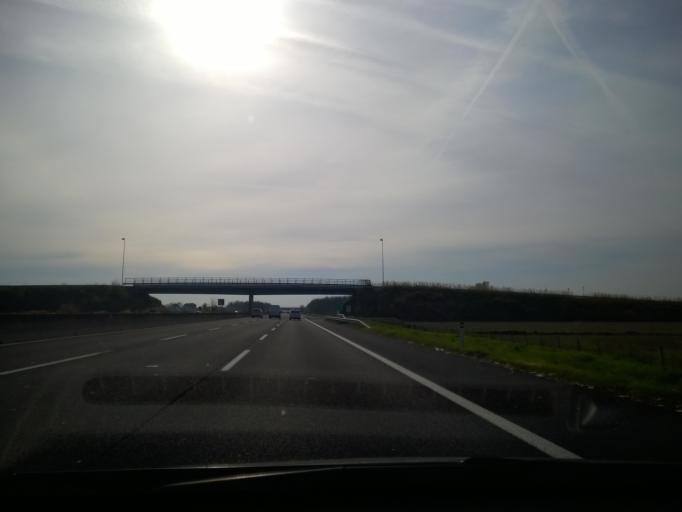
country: IT
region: Emilia-Romagna
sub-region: Provincia di Ravenna
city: Granarolo
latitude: 44.3029
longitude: 11.9554
